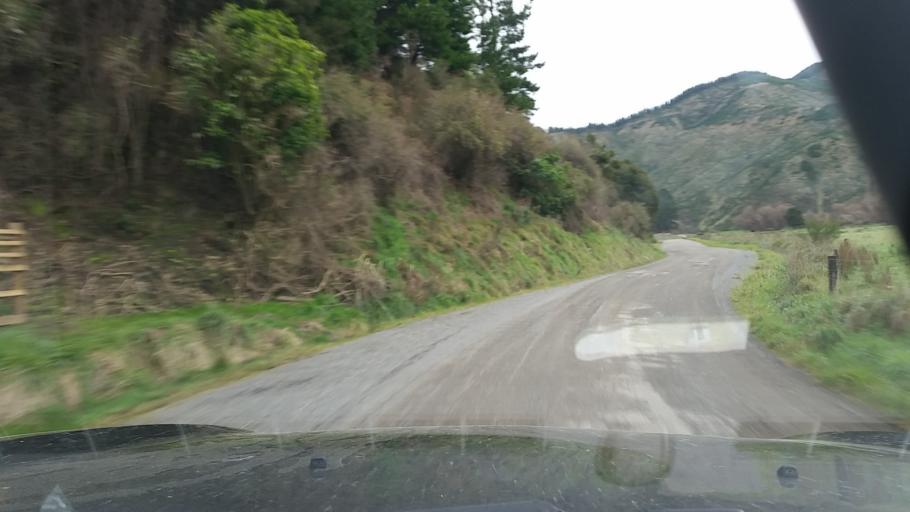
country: NZ
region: Marlborough
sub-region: Marlborough District
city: Blenheim
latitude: -41.4227
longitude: 173.8905
